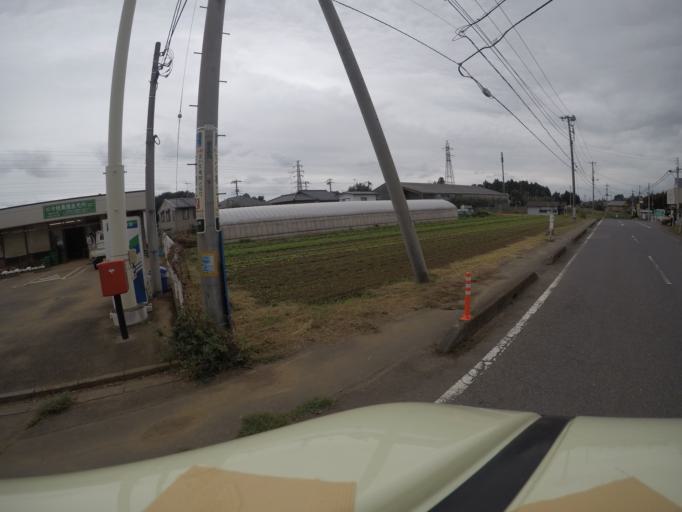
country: JP
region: Ibaraki
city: Naka
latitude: 36.0690
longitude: 140.1675
